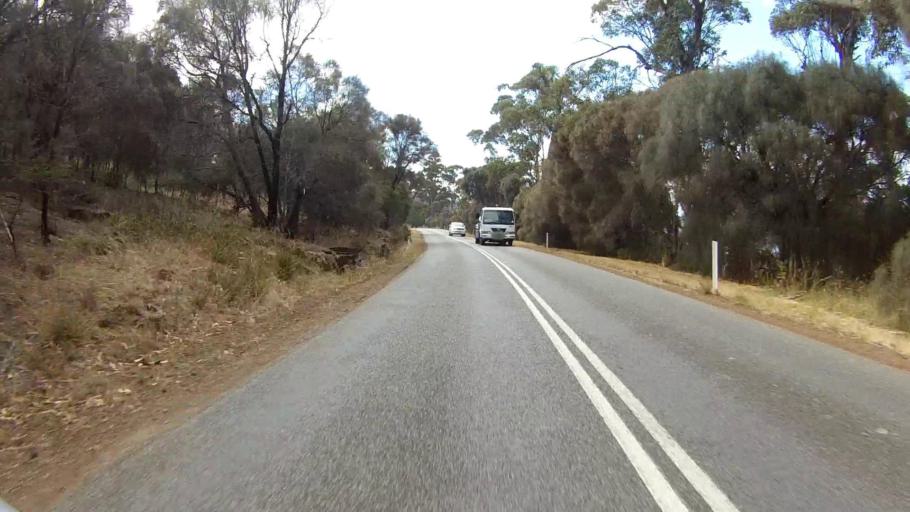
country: AU
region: Tasmania
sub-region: Sorell
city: Sorell
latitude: -42.2364
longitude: 148.0158
